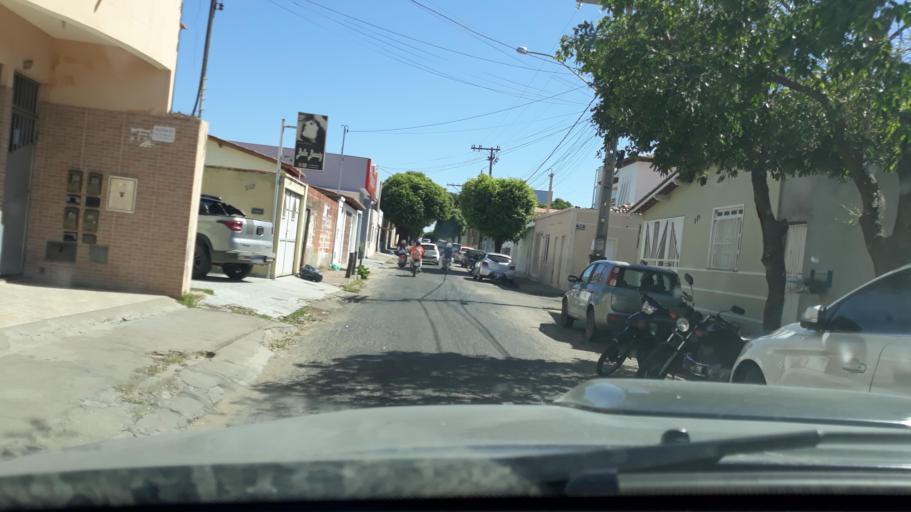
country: BR
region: Bahia
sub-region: Guanambi
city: Guanambi
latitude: -14.2266
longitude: -42.7848
